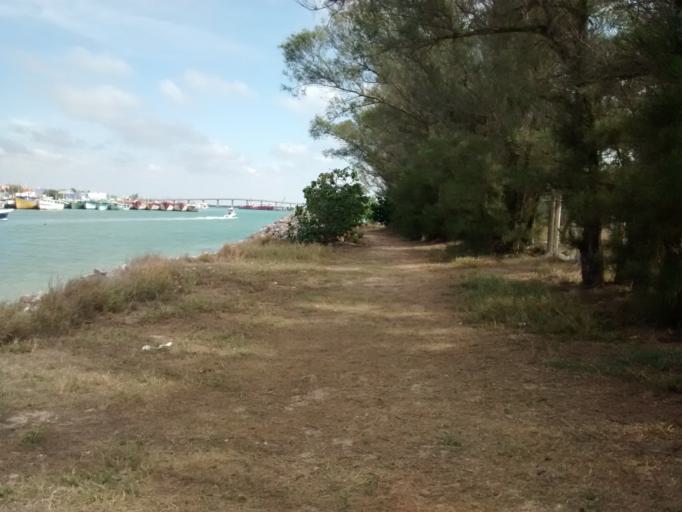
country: MX
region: Yucatan
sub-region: Progreso
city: Chelem
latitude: 21.2790
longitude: -89.7032
